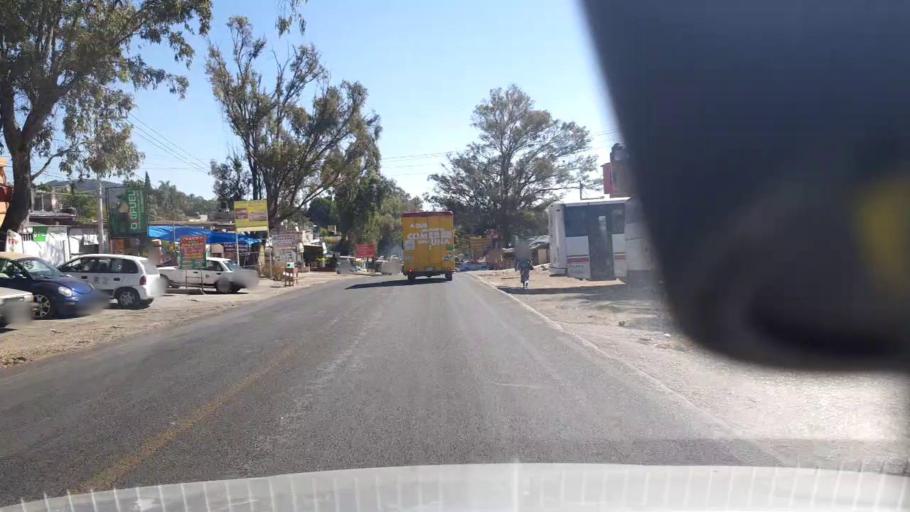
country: MX
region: Morelos
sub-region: Cuernavaca
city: Lomas de Ahuatepec
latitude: 18.9695
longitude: -99.2165
